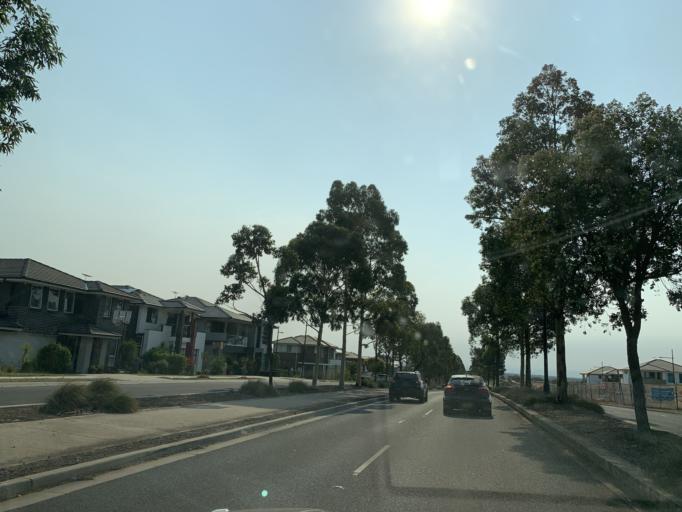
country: AU
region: New South Wales
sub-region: Blacktown
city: Quakers Hill
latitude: -33.7130
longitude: 150.8988
